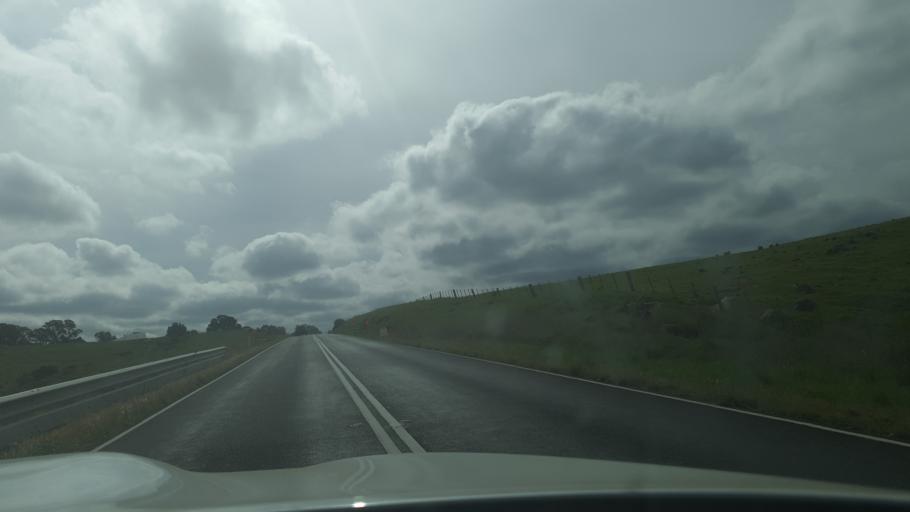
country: AU
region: Victoria
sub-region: Central Goldfields
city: Maryborough
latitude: -37.2125
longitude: 143.7252
